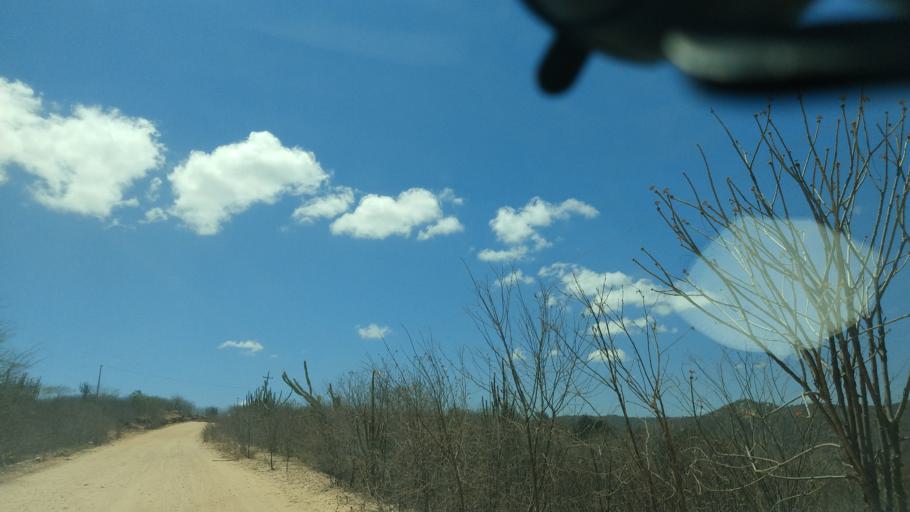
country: BR
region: Rio Grande do Norte
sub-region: Cerro Cora
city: Cerro Cora
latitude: -6.0126
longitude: -36.3024
